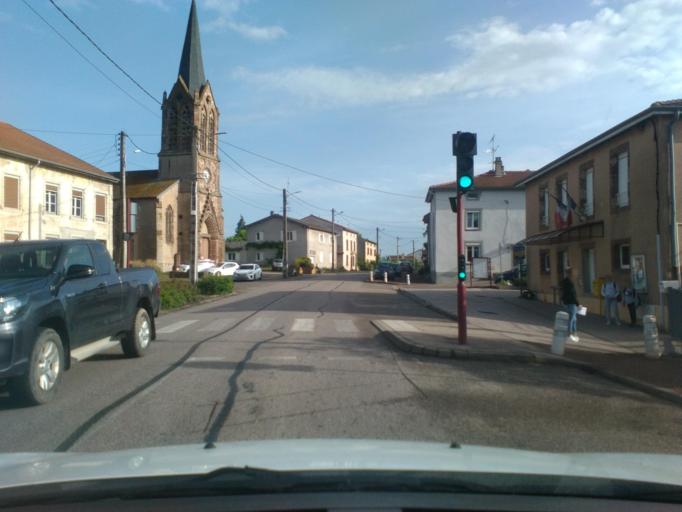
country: FR
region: Lorraine
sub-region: Departement de Meurthe-et-Moselle
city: Gerbeviller
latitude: 48.5327
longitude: 6.4615
